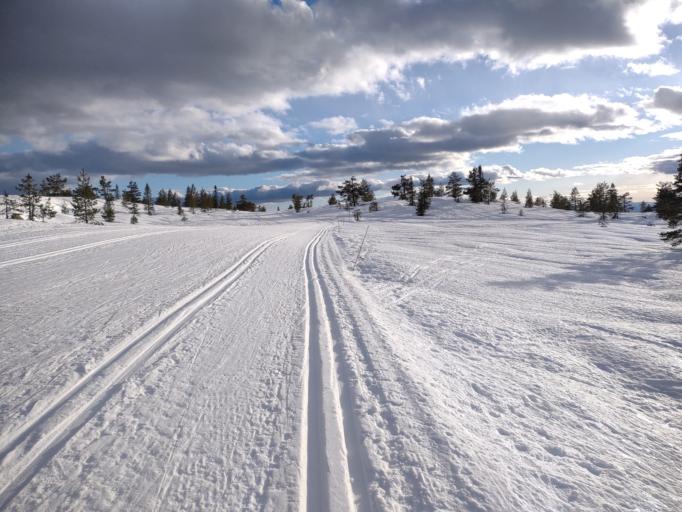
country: NO
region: Buskerud
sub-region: Flesberg
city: Lampeland
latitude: 59.7605
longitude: 9.4044
